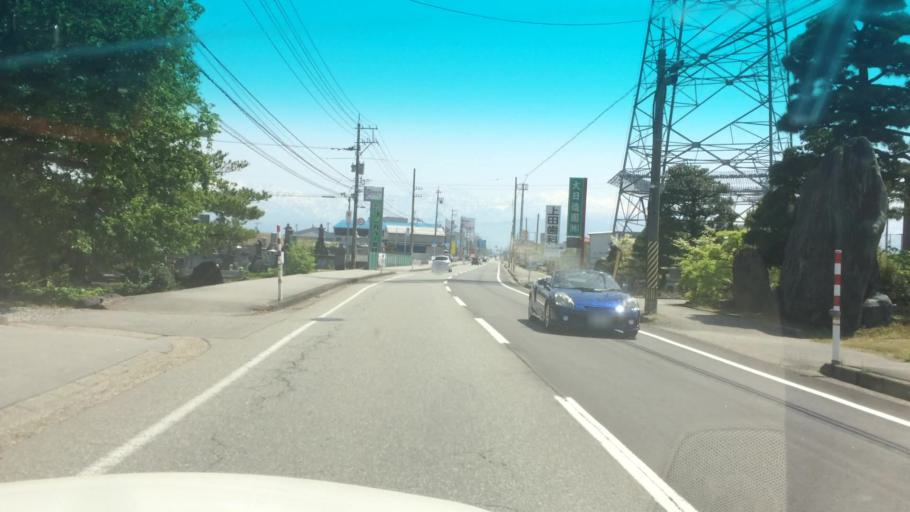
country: JP
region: Toyama
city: Toyama-shi
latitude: 36.6745
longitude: 137.2599
